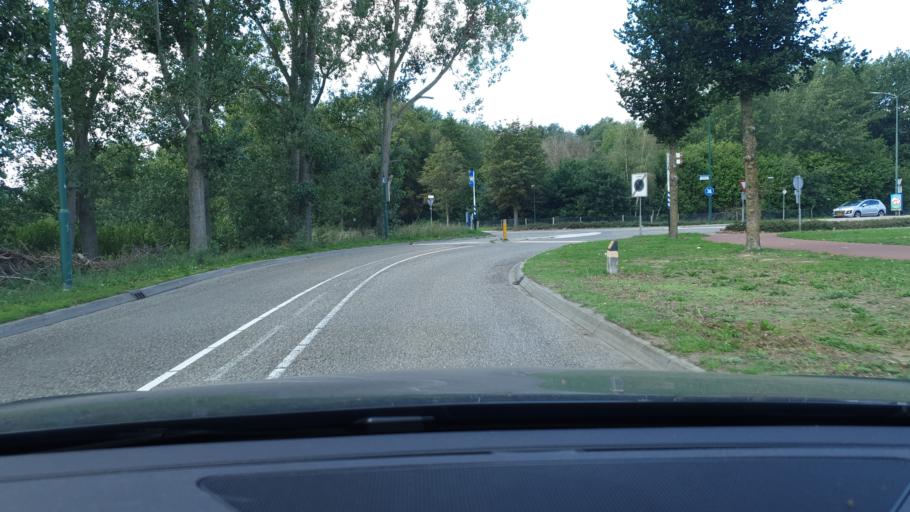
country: NL
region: North Brabant
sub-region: Gemeente Cuijk
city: Cuijk
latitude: 51.7307
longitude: 5.8586
